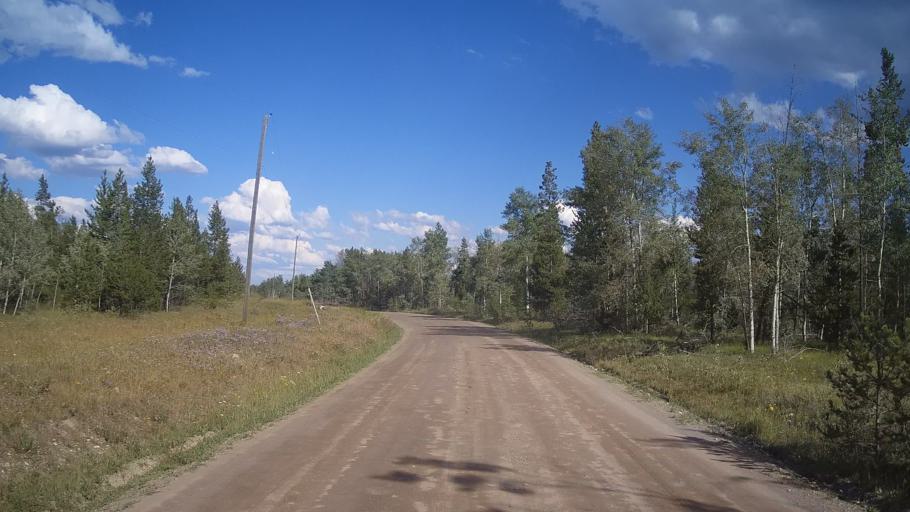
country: CA
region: British Columbia
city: Cache Creek
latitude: 51.2586
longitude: -121.6880
